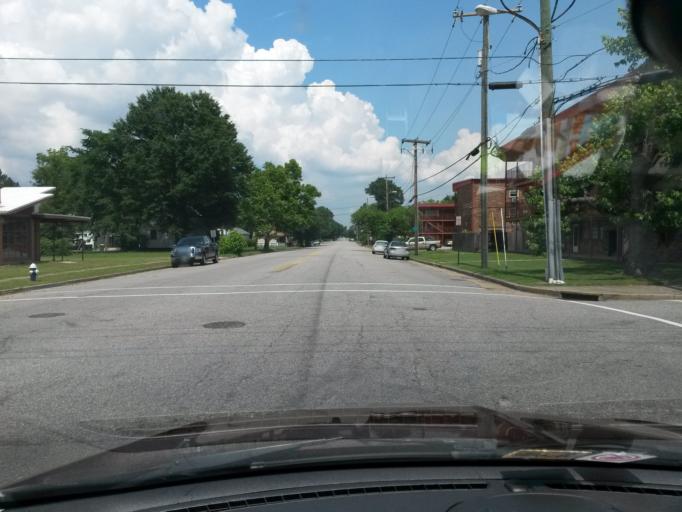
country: US
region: Virginia
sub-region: City of Hopewell
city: Hopewell
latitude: 37.3064
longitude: -77.2855
